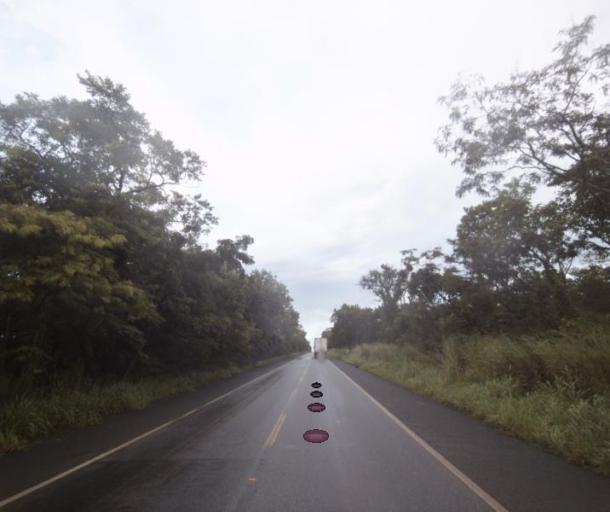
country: BR
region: Goias
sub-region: Porangatu
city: Porangatu
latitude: -13.7786
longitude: -49.0320
